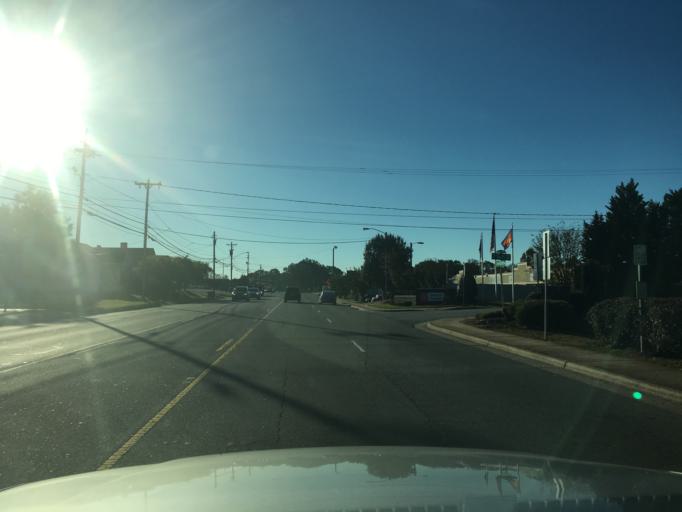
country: US
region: North Carolina
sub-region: Catawba County
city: Hickory
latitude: 35.7273
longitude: -81.3237
